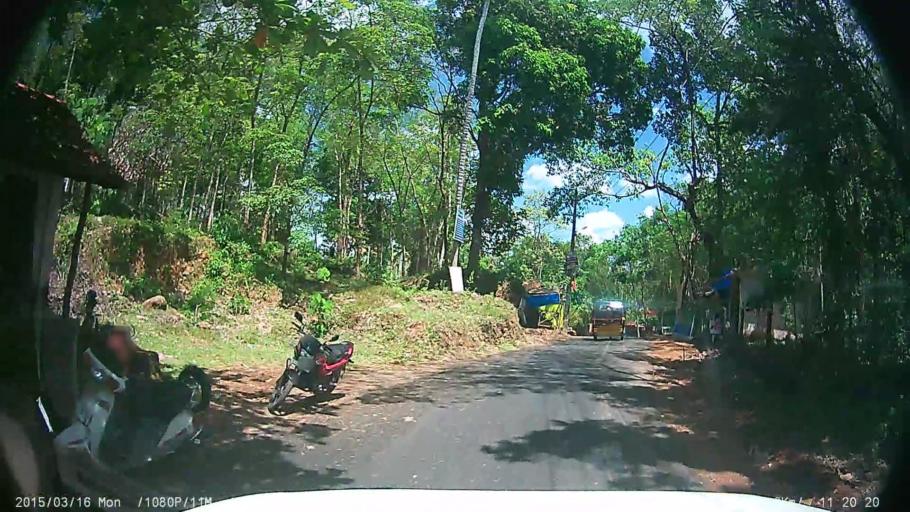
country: IN
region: Kerala
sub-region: Kottayam
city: Palackattumala
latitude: 9.7856
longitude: 76.5523
